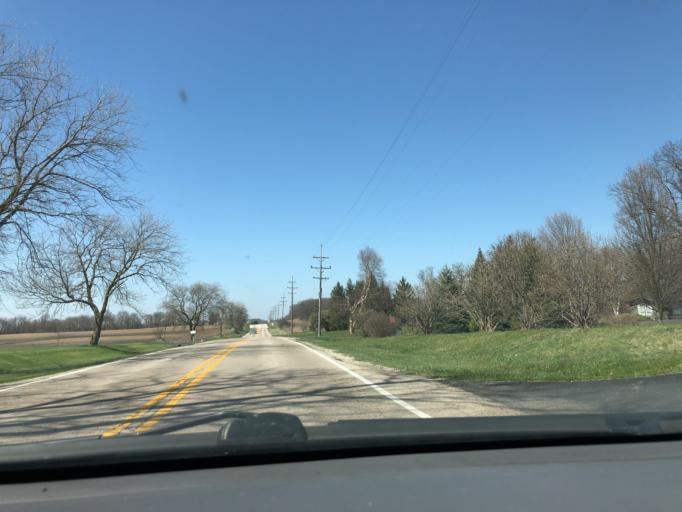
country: US
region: Illinois
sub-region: Kane County
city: Hampshire
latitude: 42.1140
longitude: -88.4912
